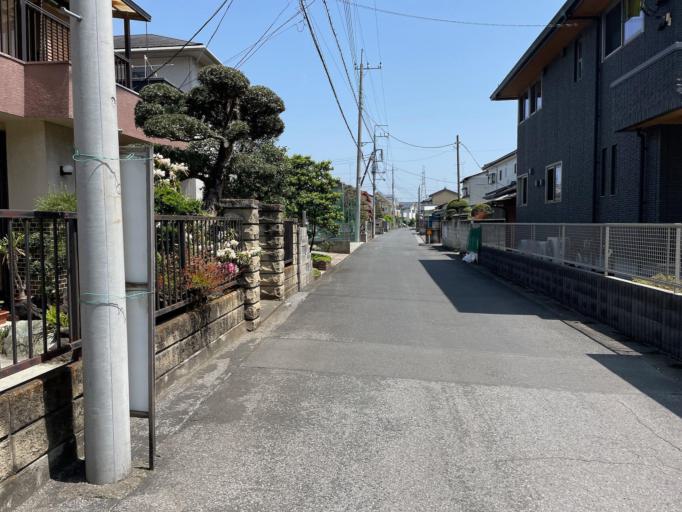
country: JP
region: Tochigi
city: Ashikaga
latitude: 36.3101
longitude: 139.4539
